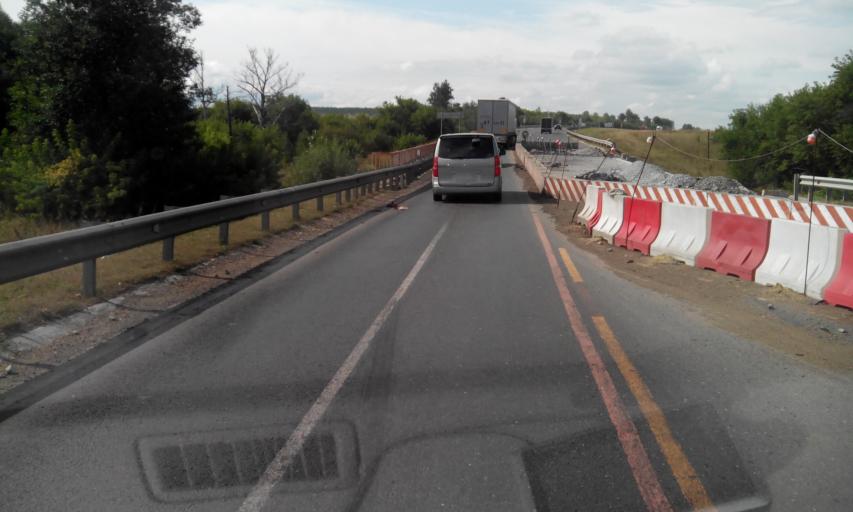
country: RU
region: Ulyanovsk
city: Nikolayevka
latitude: 53.1161
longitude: 47.1731
